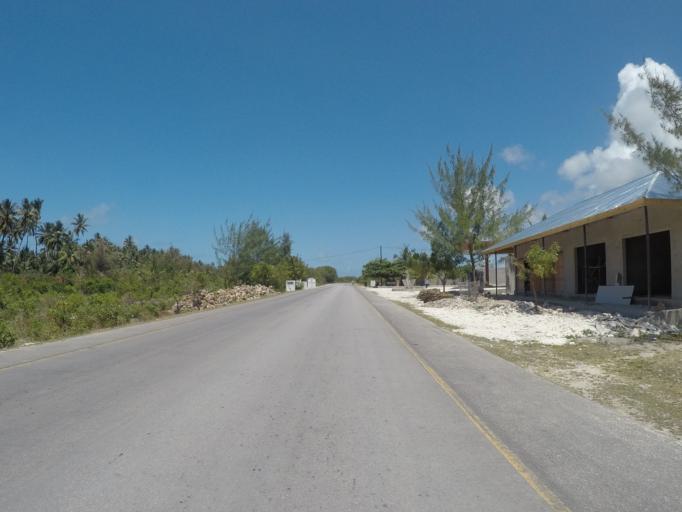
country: TZ
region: Zanzibar Central/South
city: Nganane
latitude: -6.3223
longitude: 39.5447
